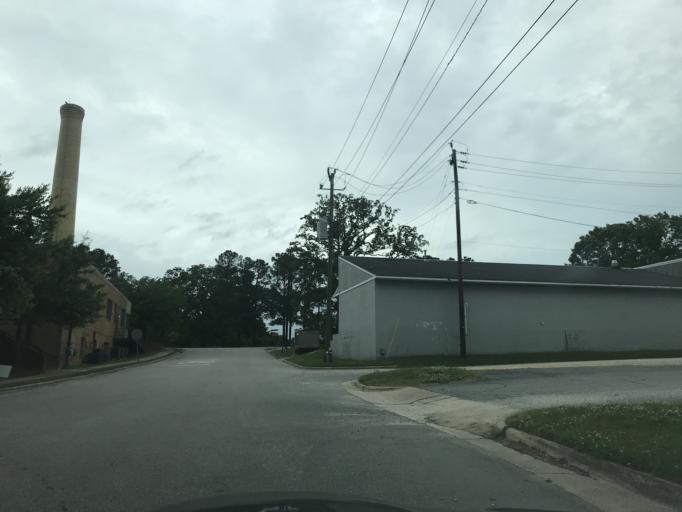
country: US
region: North Carolina
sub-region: Wake County
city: West Raleigh
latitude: 35.7933
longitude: -78.6880
